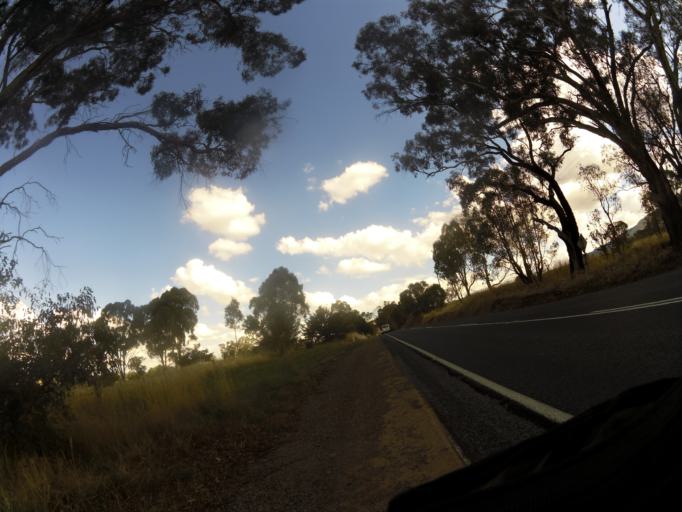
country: AU
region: Victoria
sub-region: Mansfield
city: Mansfield
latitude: -36.9362
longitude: 145.9994
